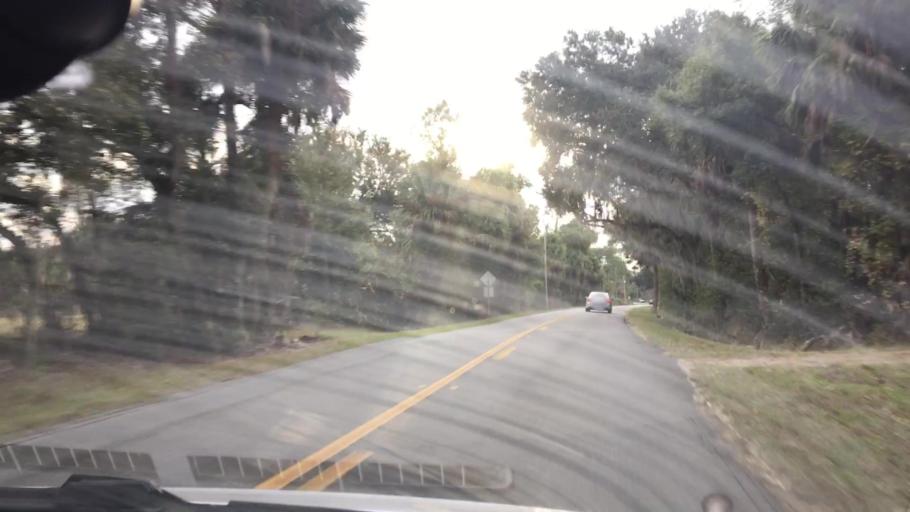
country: US
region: Florida
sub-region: Seminole County
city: Midway
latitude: 28.8504
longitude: -81.2053
